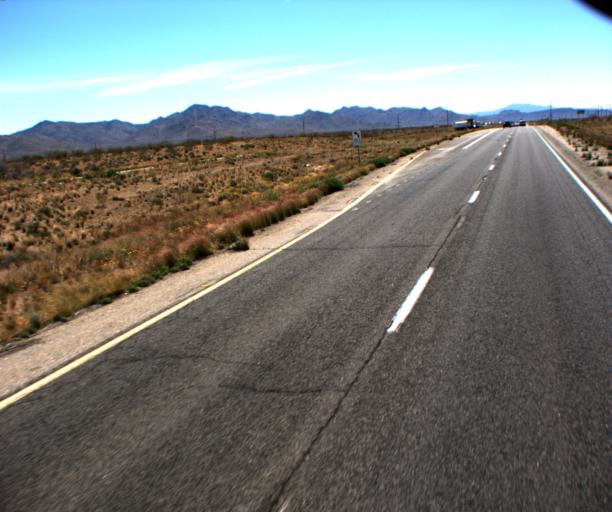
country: US
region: Arizona
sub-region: Mohave County
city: Golden Valley
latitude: 35.3244
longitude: -114.2072
